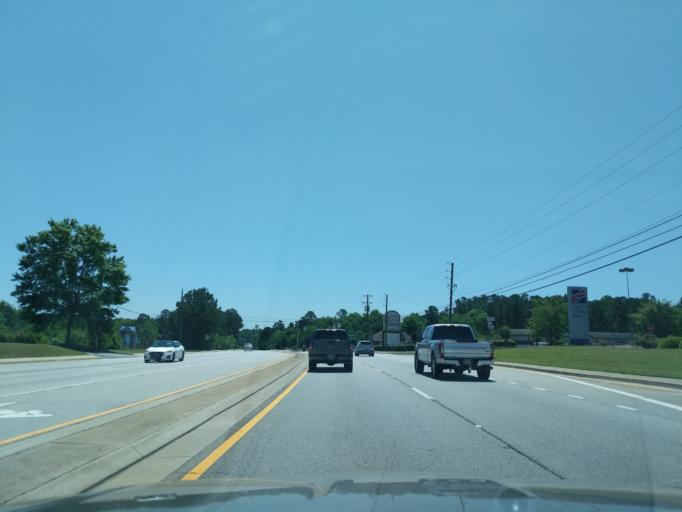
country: US
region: Georgia
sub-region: Columbia County
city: Martinez
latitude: 33.5276
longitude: -82.0731
